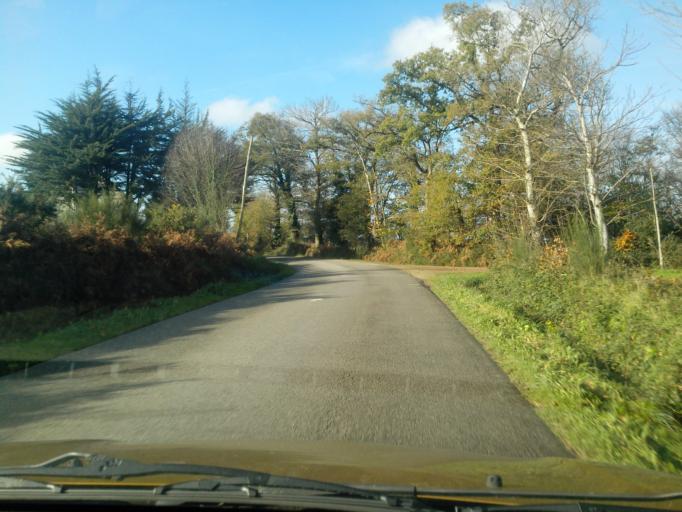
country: FR
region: Brittany
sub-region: Departement du Morbihan
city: Molac
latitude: 47.7311
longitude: -2.4281
